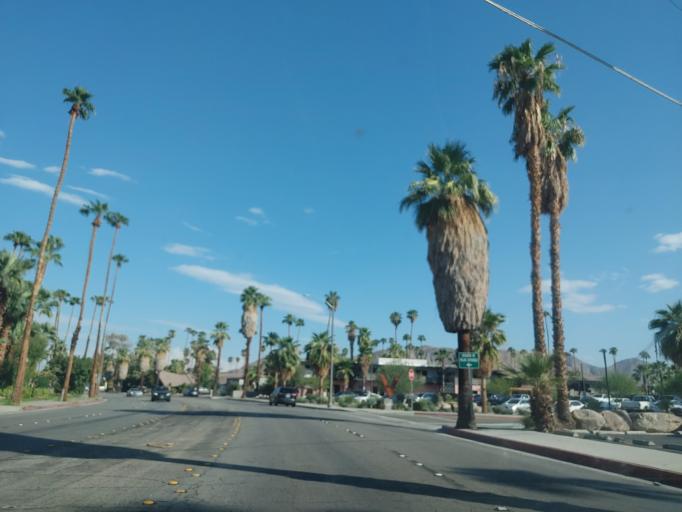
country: US
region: California
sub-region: Riverside County
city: Palm Springs
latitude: 33.8016
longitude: -116.5445
